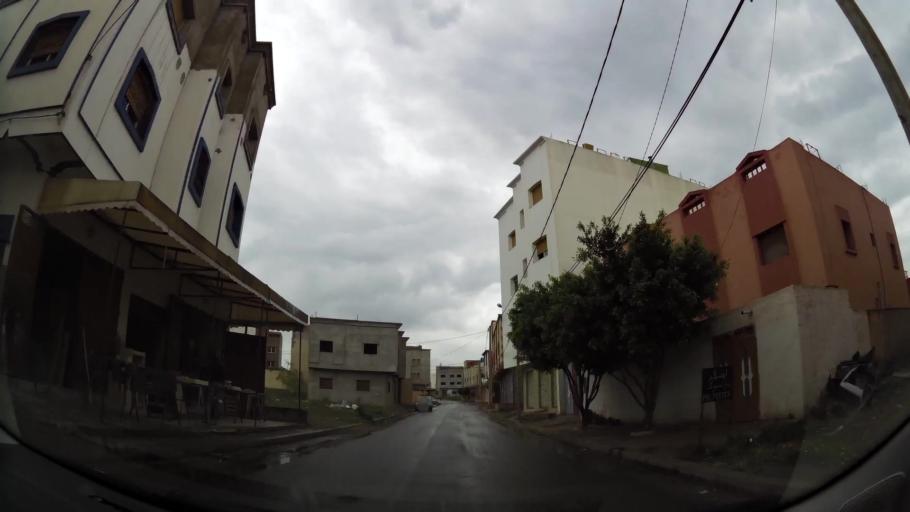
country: MA
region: Oriental
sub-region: Nador
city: Nador
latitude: 35.1496
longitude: -2.9906
